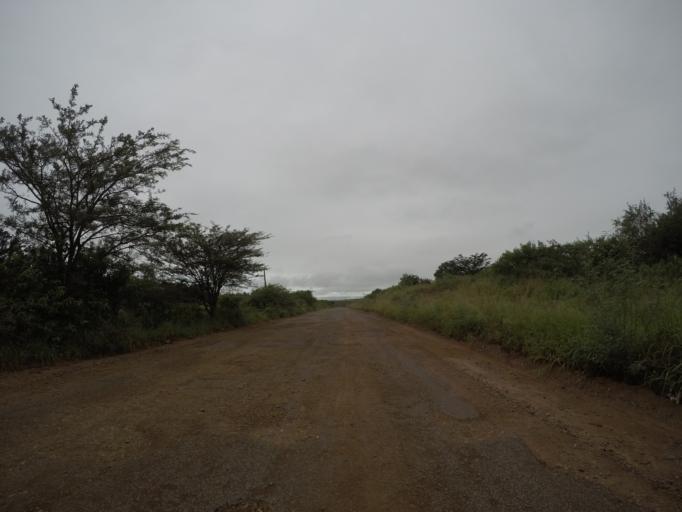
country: ZA
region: KwaZulu-Natal
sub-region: uThungulu District Municipality
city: Empangeni
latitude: -28.6599
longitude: 31.7852
